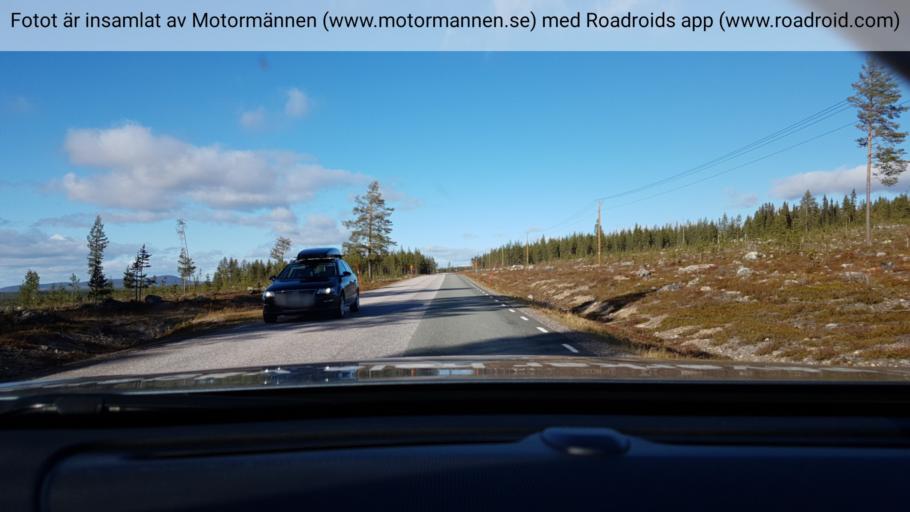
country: SE
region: Vaesterbotten
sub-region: Mala Kommun
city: Mala
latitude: 65.7720
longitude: 18.5299
